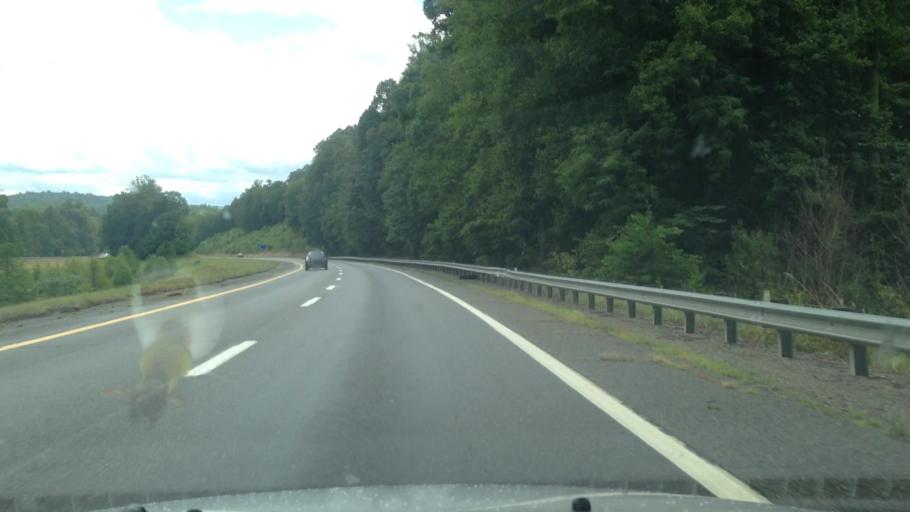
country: US
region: Virginia
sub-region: Henry County
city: Stanleytown
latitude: 36.7067
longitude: -79.9574
